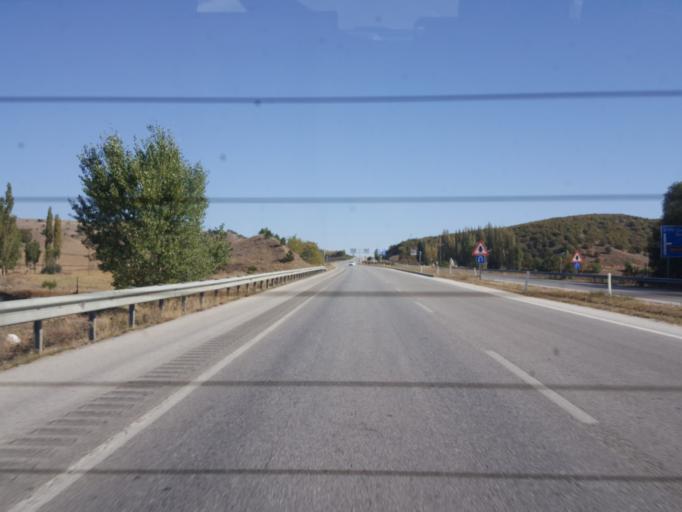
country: TR
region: Corum
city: Alaca
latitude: 40.2723
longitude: 34.6401
